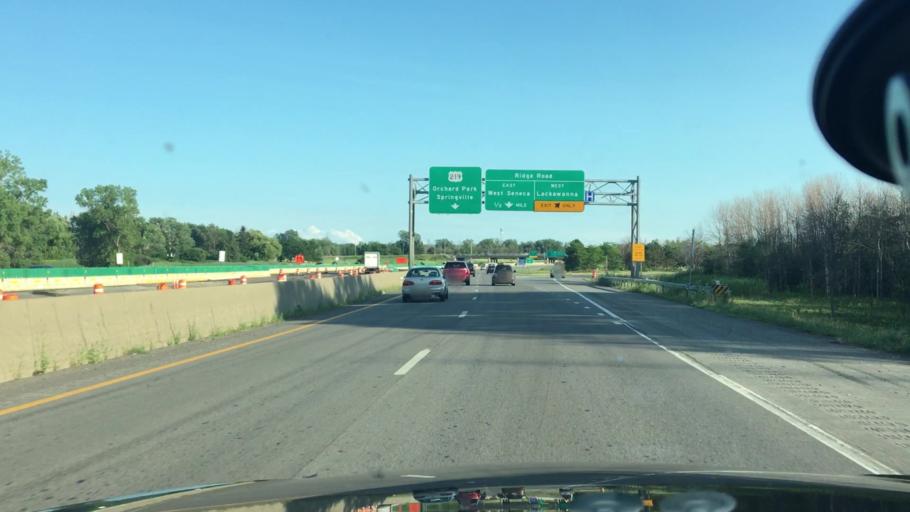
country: US
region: New York
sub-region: Erie County
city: West Seneca
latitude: 42.8336
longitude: -78.7930
